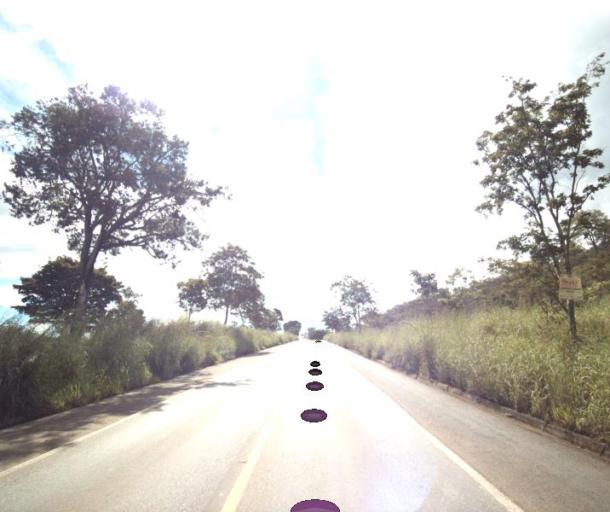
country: BR
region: Goias
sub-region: Petrolina De Goias
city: Petrolina de Goias
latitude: -15.9504
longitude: -49.1876
